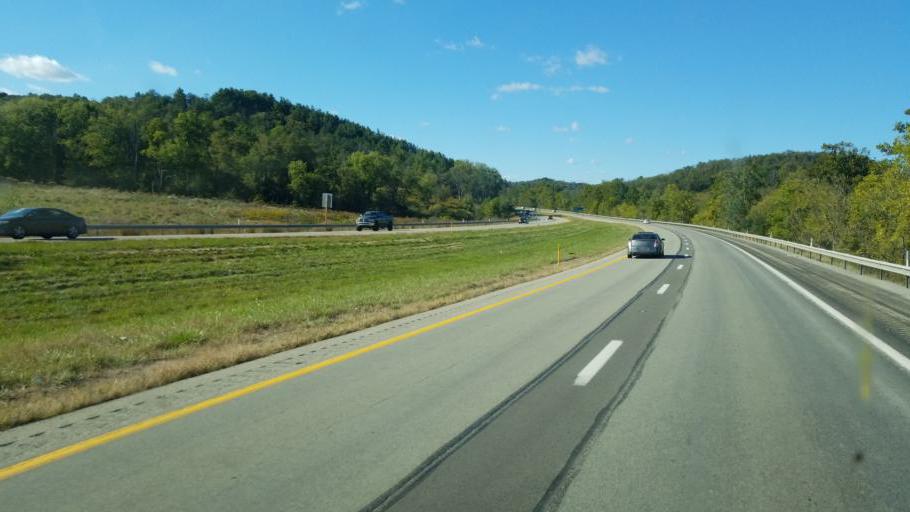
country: US
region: Pennsylvania
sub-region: Washington County
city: East Washington
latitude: 40.0978
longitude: -80.1934
